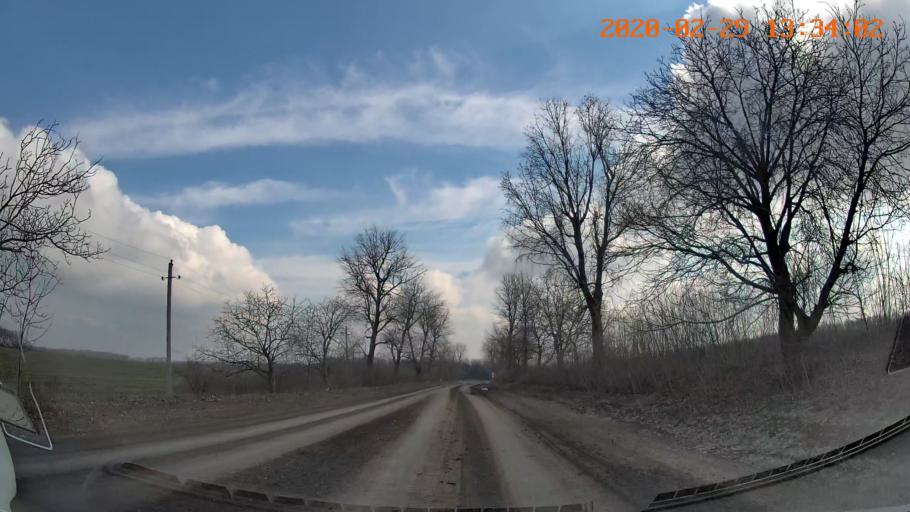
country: MD
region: Telenesti
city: Camenca
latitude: 47.8708
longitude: 28.6201
